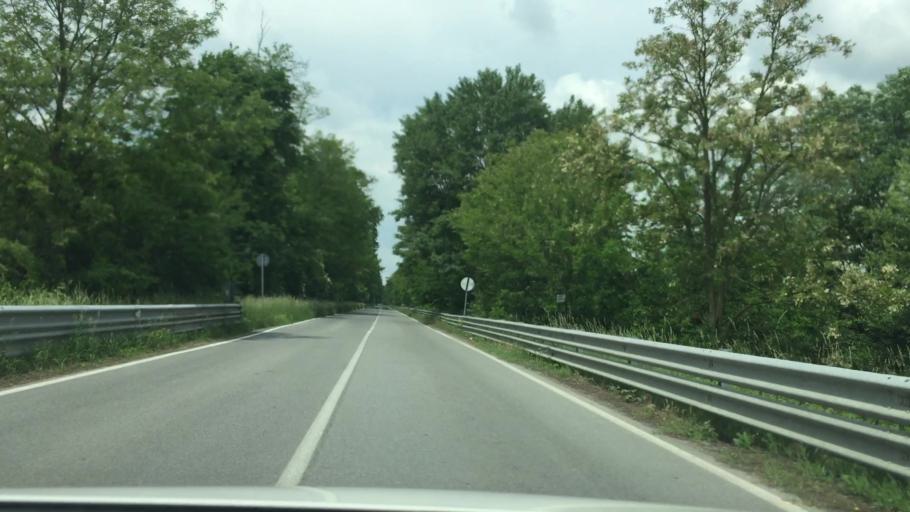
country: IT
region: Lombardy
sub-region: Provincia di Varese
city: Lonate Pozzolo
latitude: 45.5661
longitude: 8.7497
